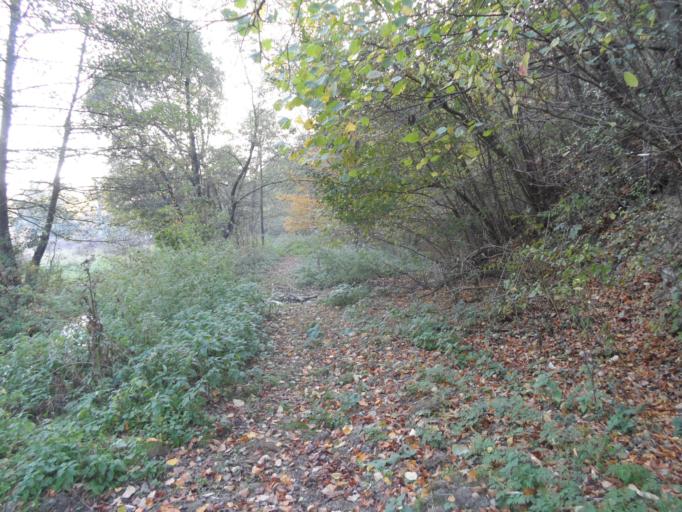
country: HU
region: Veszprem
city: Ajka
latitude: 47.2315
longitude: 17.5854
